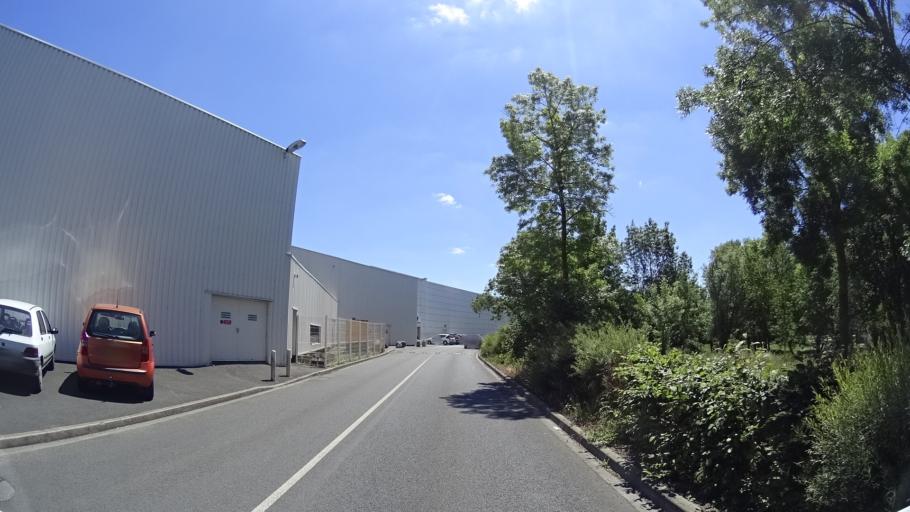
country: FR
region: Pays de la Loire
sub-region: Departement de Maine-et-Loire
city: Saumur
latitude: 47.2624
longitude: -0.0924
